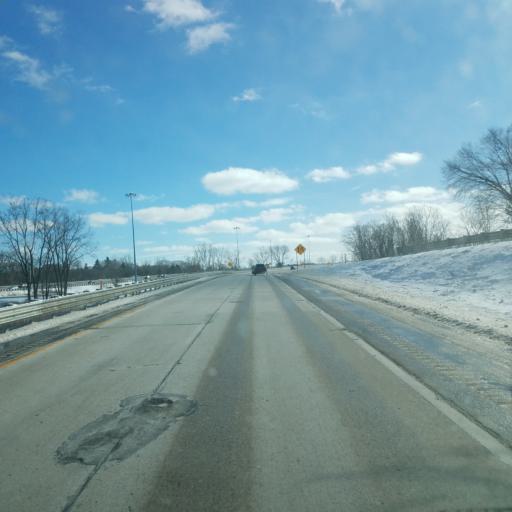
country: US
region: Michigan
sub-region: Ingham County
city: East Lansing
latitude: 42.7236
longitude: -84.5077
